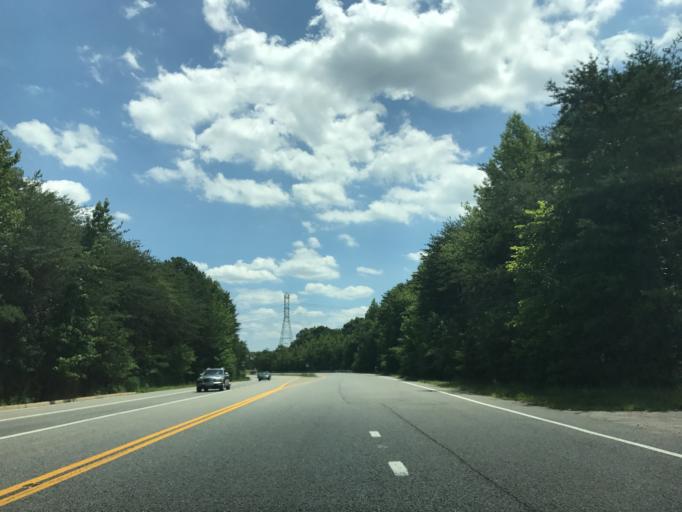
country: US
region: Maryland
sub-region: Prince George's County
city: Glenn Dale
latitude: 39.0214
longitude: -76.7694
